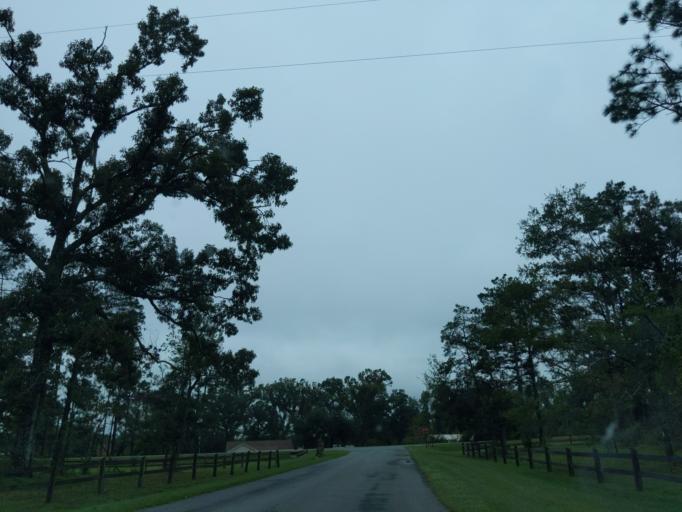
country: US
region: Florida
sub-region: Jackson County
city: Sneads
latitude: 30.7391
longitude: -84.9363
